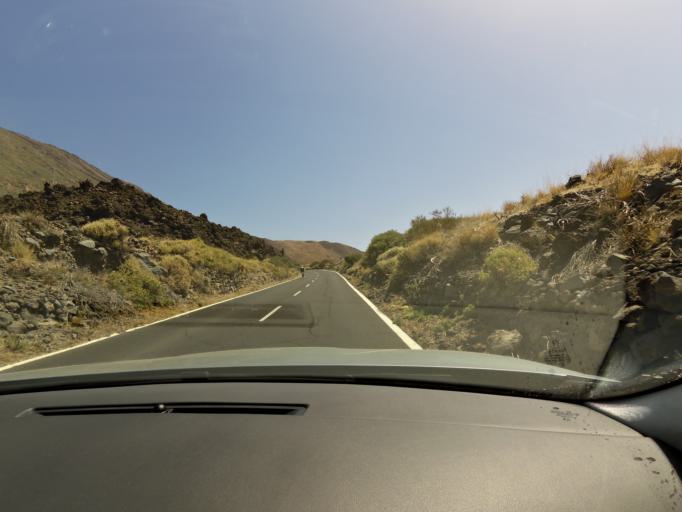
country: ES
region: Canary Islands
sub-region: Provincia de Santa Cruz de Tenerife
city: Vilaflor
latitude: 28.2461
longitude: -16.6283
